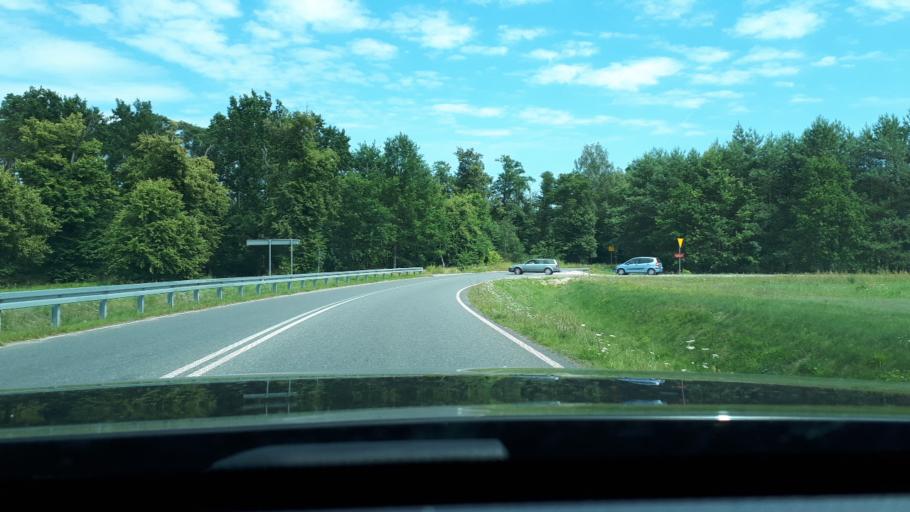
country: PL
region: Lodz Voivodeship
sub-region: powiat Lowicki
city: Bobrowniki
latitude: 52.0733
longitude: 20.0389
